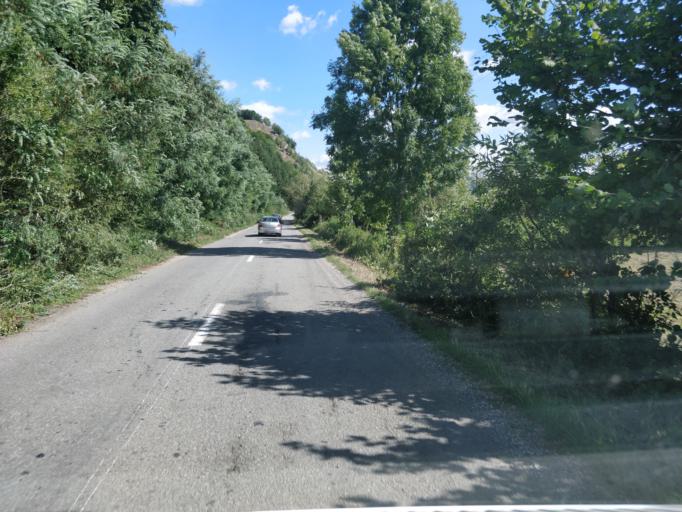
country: RO
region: Cluj
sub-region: Comuna Sacueu
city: Sacuieu
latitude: 46.8699
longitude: 22.8754
